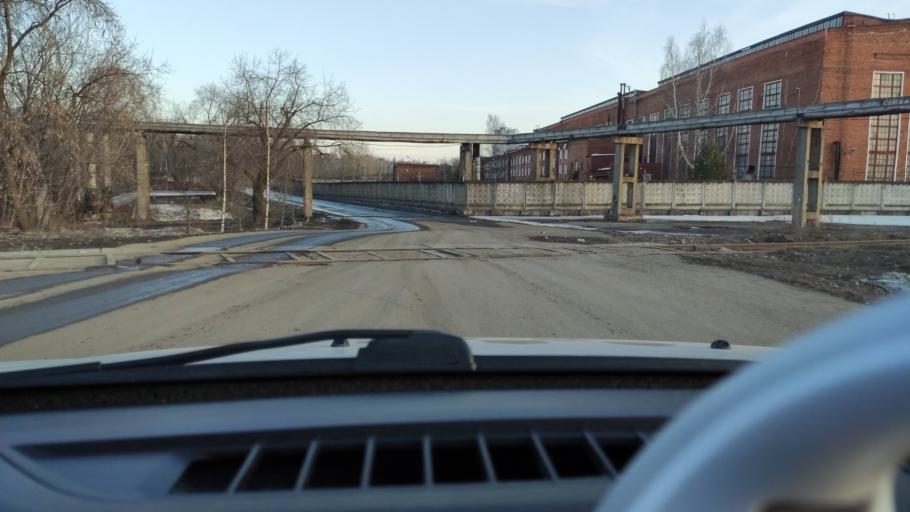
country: RU
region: Perm
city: Perm
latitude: 58.0405
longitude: 56.3060
